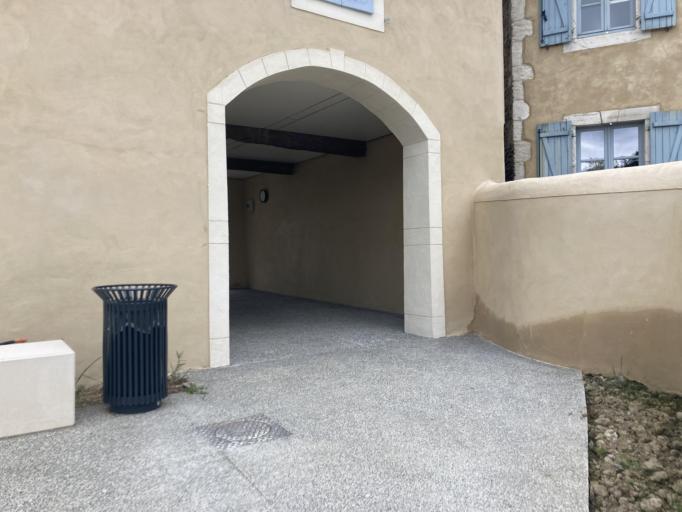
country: FR
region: Aquitaine
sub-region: Departement des Pyrenees-Atlantiques
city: Lescar
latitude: 43.3325
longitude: -0.4303
